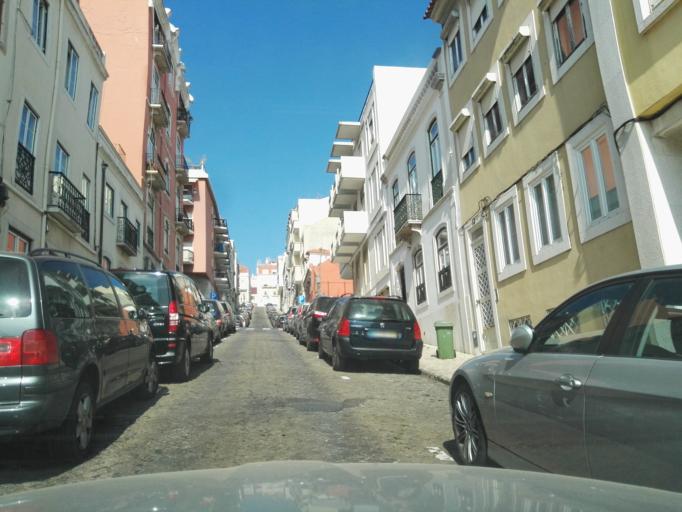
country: PT
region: Setubal
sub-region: Almada
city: Cacilhas
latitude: 38.7082
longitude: -9.1604
